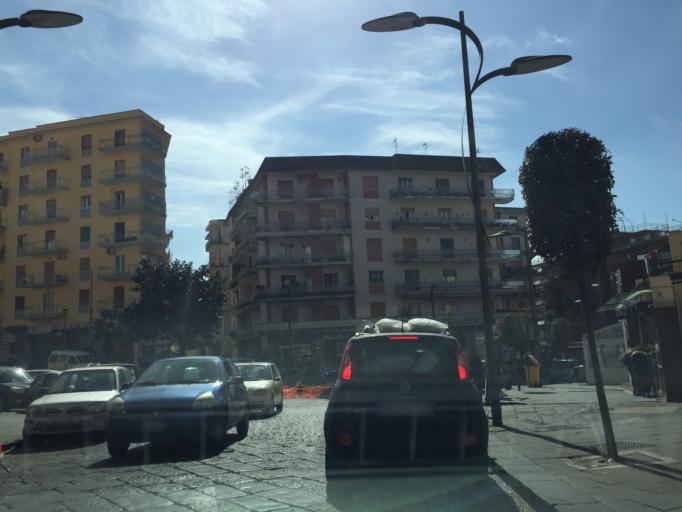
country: IT
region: Campania
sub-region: Provincia di Napoli
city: Ercolano
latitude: 40.8089
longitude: 14.3537
